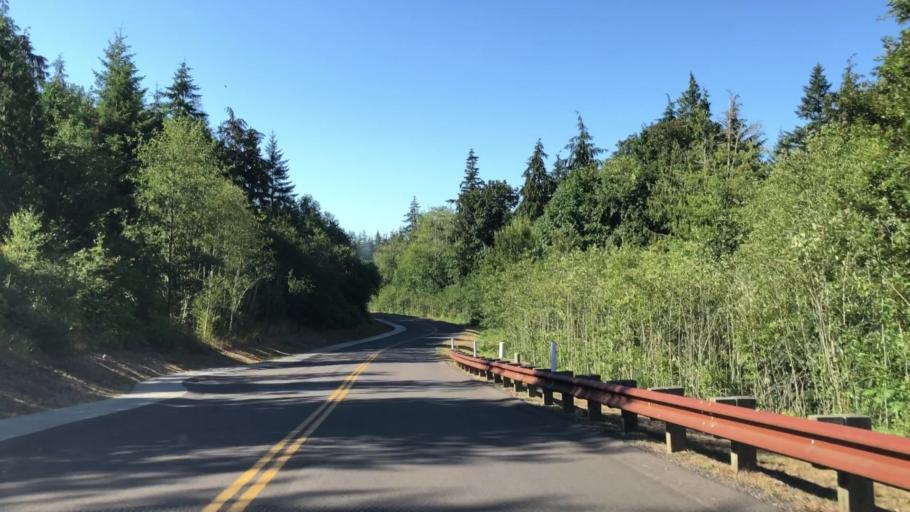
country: US
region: Washington
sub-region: Kitsap County
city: Indianola
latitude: 47.7716
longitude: -122.5252
